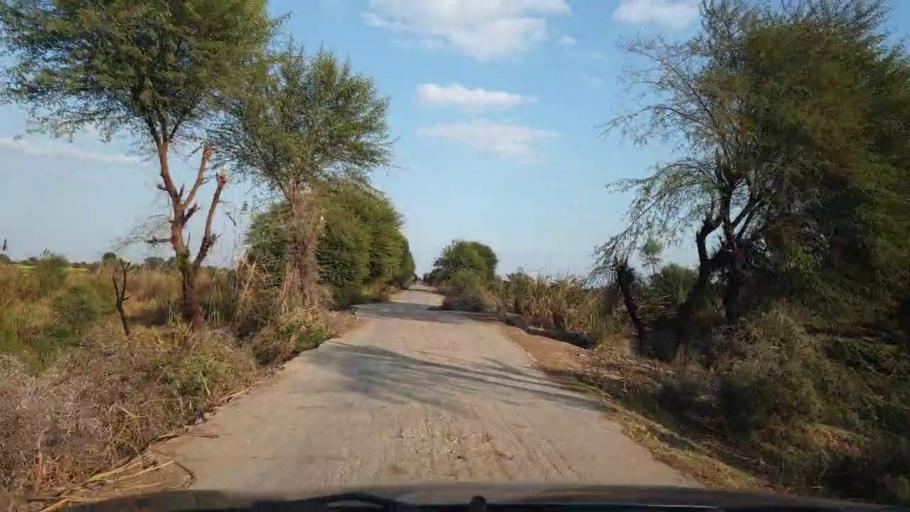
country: PK
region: Sindh
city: Sinjhoro
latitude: 25.9952
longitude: 68.7452
